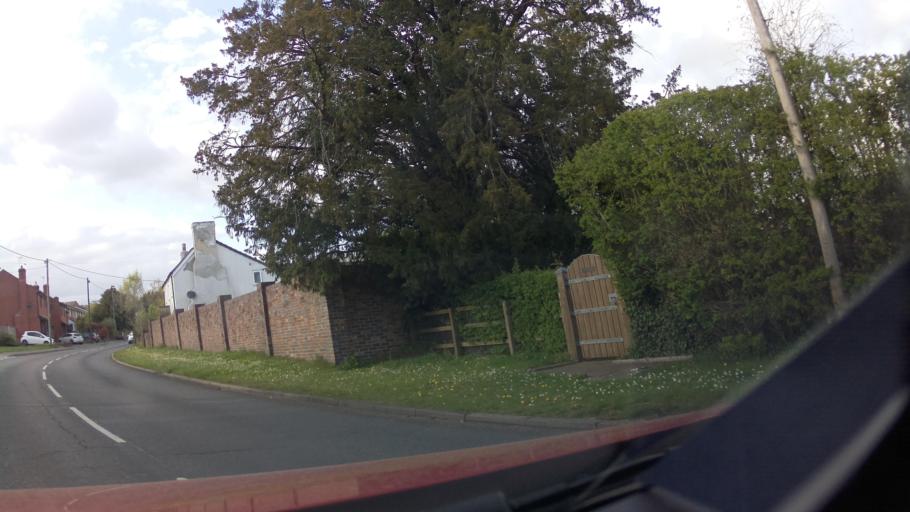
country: GB
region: England
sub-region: Hampshire
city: Colden Common
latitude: 50.9697
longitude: -1.3003
